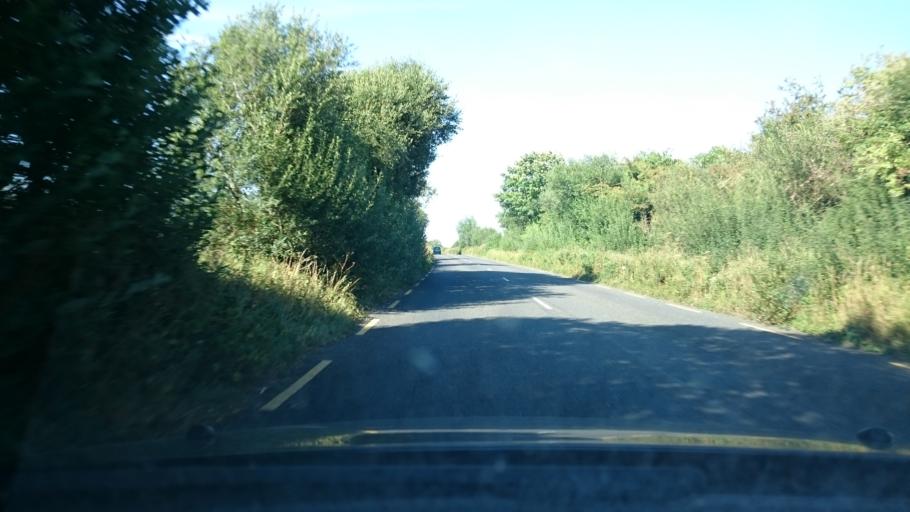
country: IE
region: Leinster
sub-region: Kilkenny
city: Graiguenamanagh
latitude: 52.5601
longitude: -6.9530
